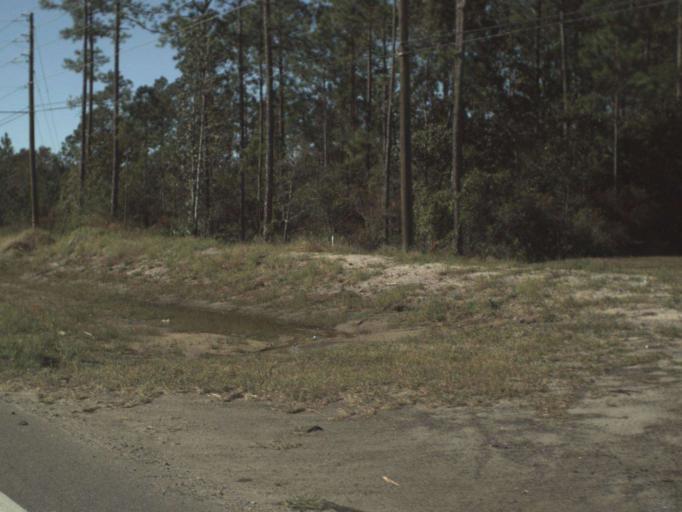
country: US
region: Florida
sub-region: Walton County
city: Freeport
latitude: 30.4810
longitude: -86.1252
